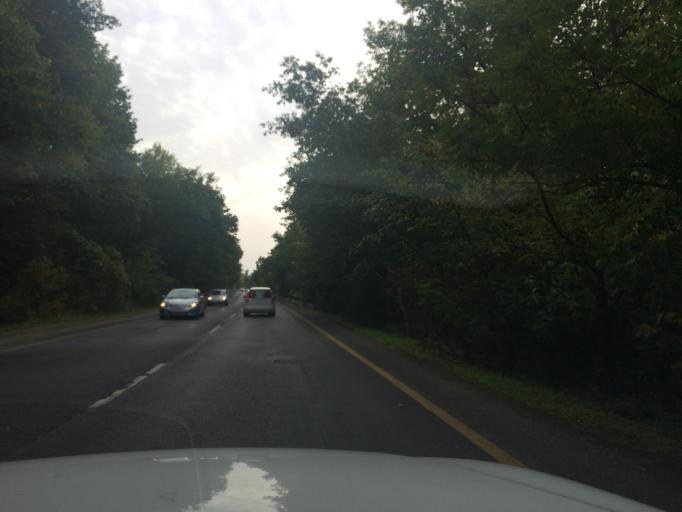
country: HU
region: Szabolcs-Szatmar-Bereg
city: Nyiregyhaza
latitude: 47.9976
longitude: 21.7231
